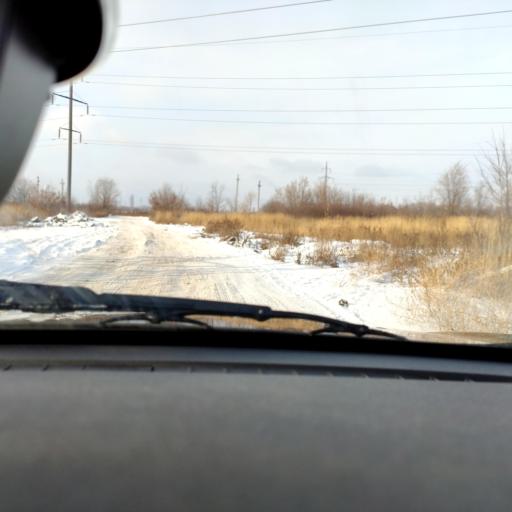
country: RU
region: Samara
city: Tol'yatti
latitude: 53.5464
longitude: 49.4290
